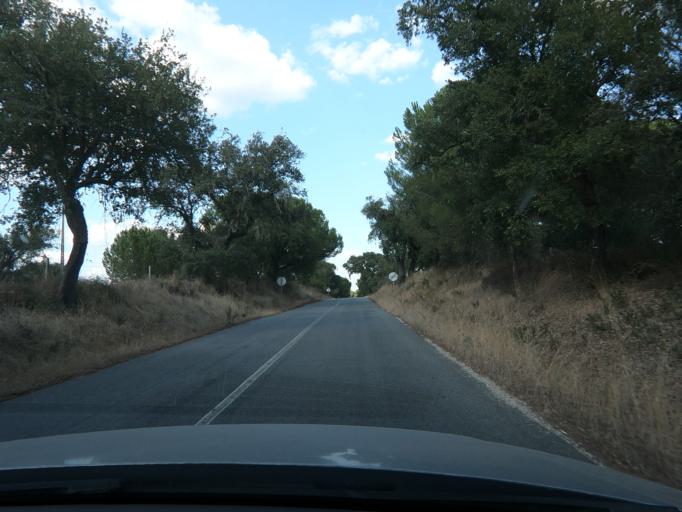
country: PT
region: Setubal
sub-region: Alcacer do Sal
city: Alcacer do Sal
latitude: 38.2582
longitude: -8.3562
